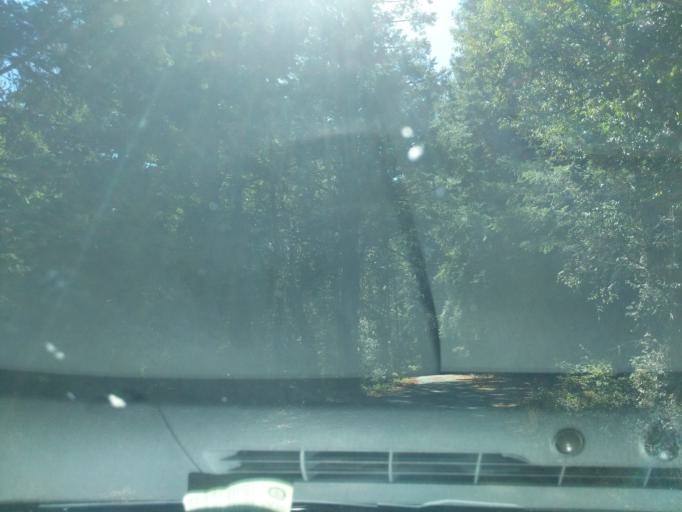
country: US
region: California
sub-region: Sonoma County
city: Monte Rio
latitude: 38.5273
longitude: -123.2271
